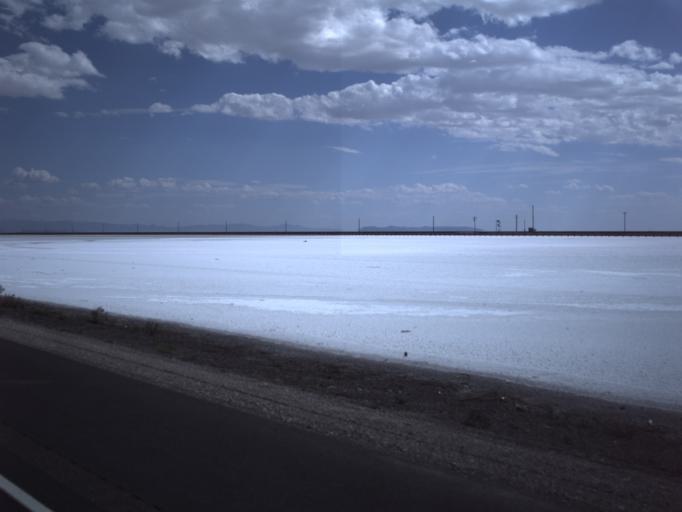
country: US
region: Utah
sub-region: Tooele County
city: Wendover
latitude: 40.7346
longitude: -113.6641
